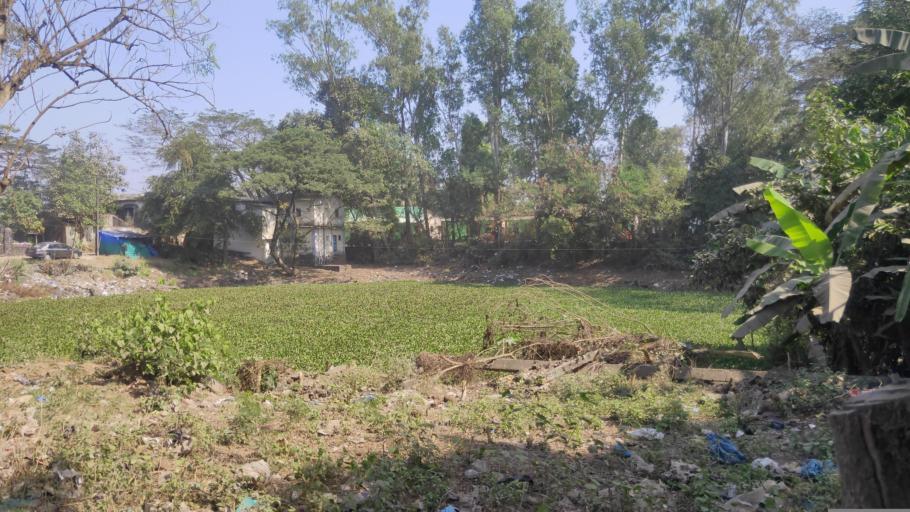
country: IN
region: Maharashtra
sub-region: Thane
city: Vada
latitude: 19.4958
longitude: 73.0372
